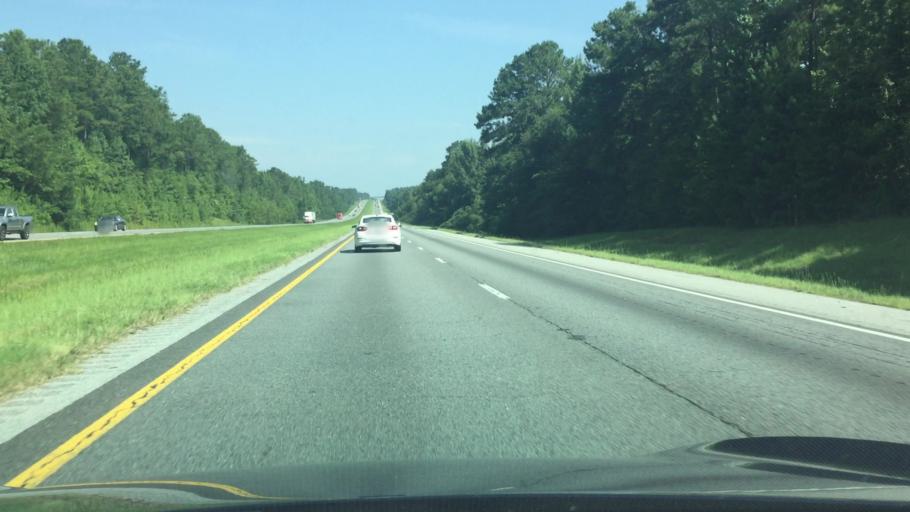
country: US
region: Alabama
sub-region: Autauga County
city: Marbury
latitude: 32.6598
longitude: -86.5012
